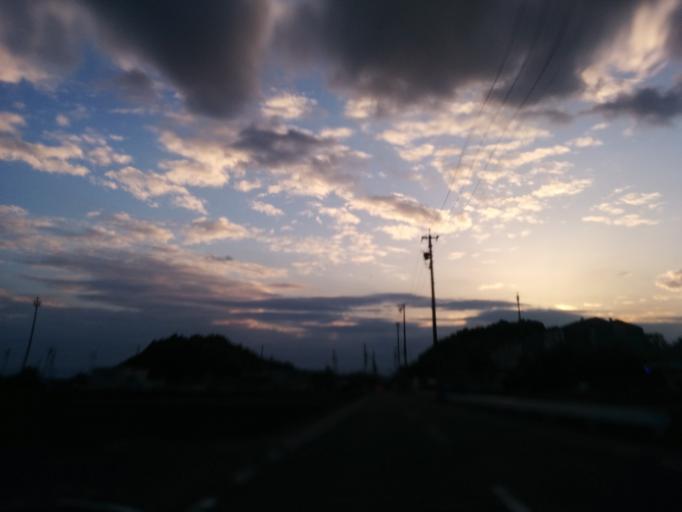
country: JP
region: Gifu
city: Kakamigahara
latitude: 35.3874
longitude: 136.8913
